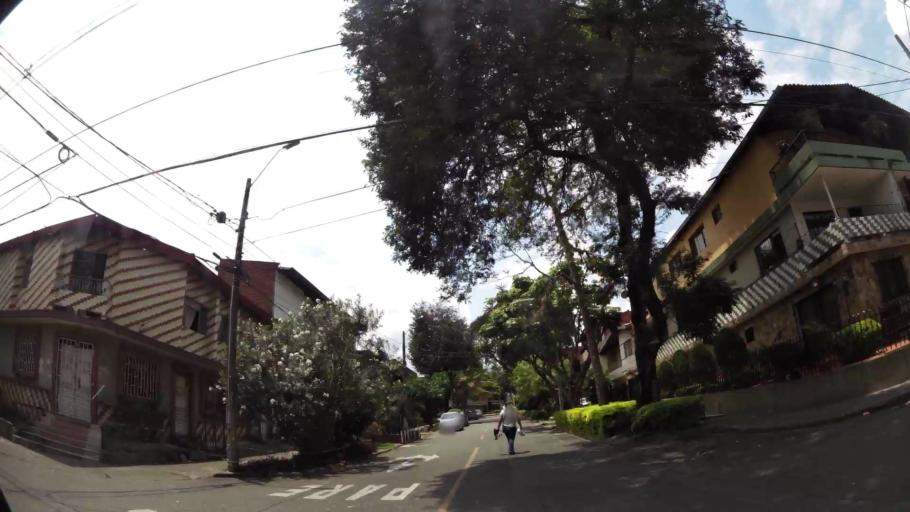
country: CO
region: Antioquia
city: Medellin
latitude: 6.2485
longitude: -75.6008
